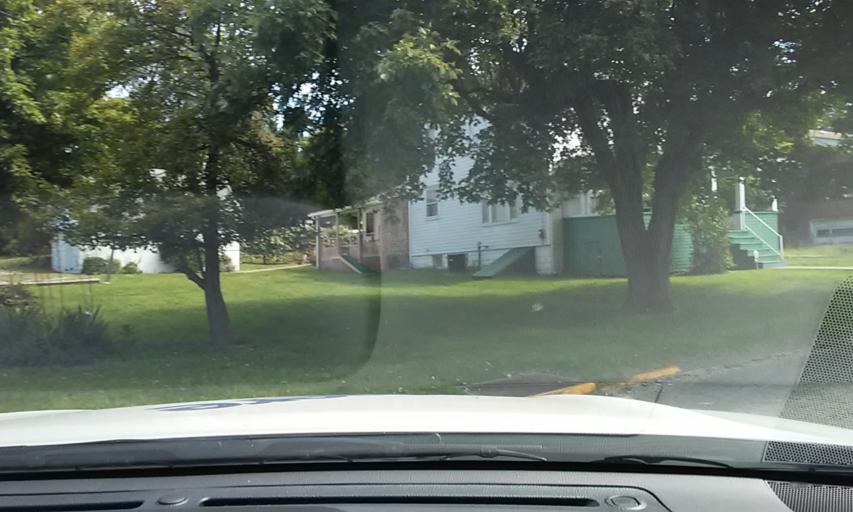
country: US
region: West Virginia
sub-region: Monongalia County
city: Westover
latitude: 39.6365
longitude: -79.9720
